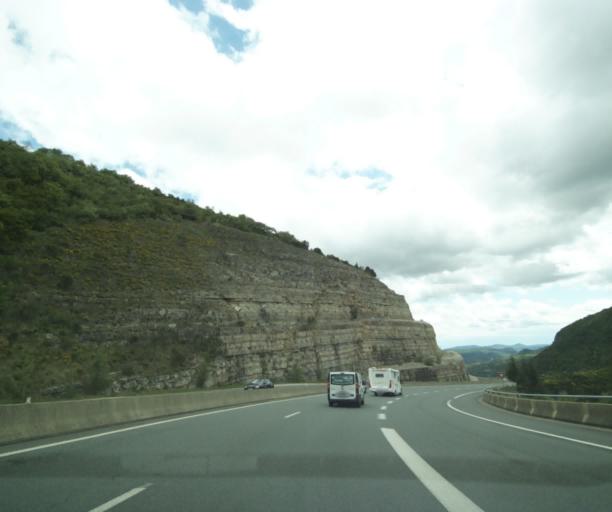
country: FR
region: Languedoc-Roussillon
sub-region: Departement de l'Herault
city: Lodeve
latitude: 43.8147
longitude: 3.3198
